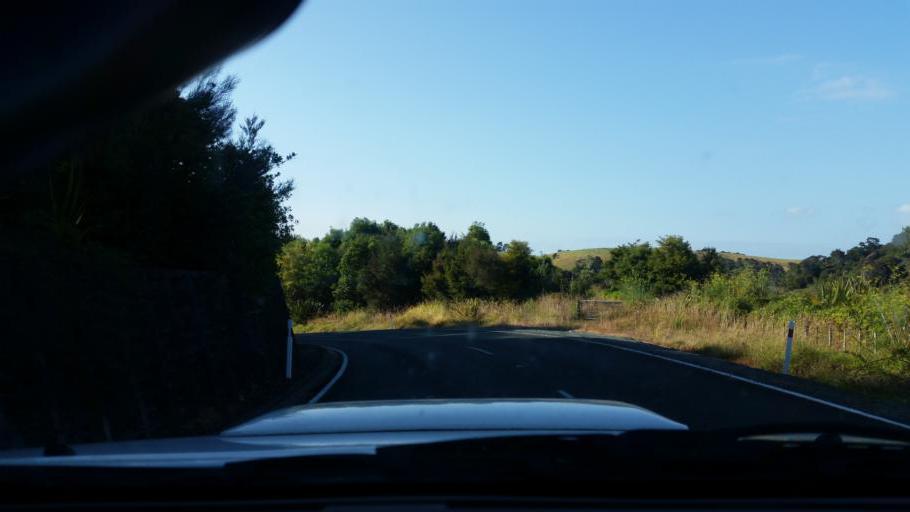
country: NZ
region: Northland
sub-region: Whangarei
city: Ruakaka
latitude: -36.1106
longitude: 174.2296
